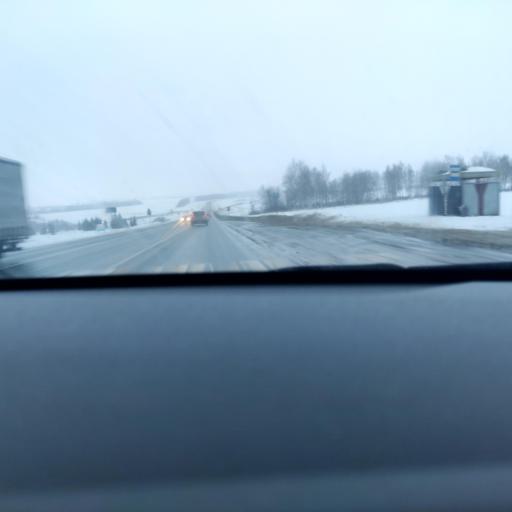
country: RU
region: Tatarstan
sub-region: Chistopol'skiy Rayon
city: Chistopol'
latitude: 55.3214
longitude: 50.4271
